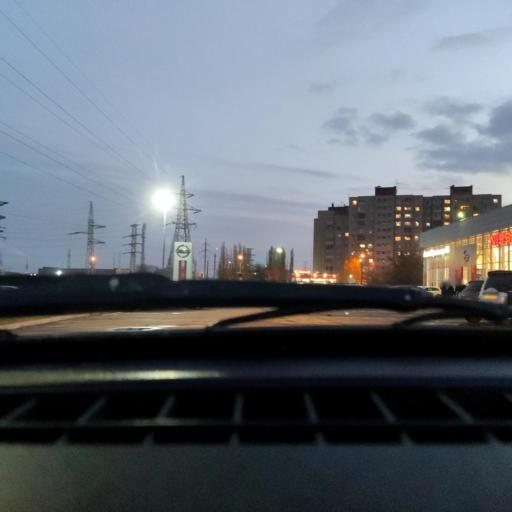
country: RU
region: Bashkortostan
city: Ufa
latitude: 54.7983
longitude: 56.0561
